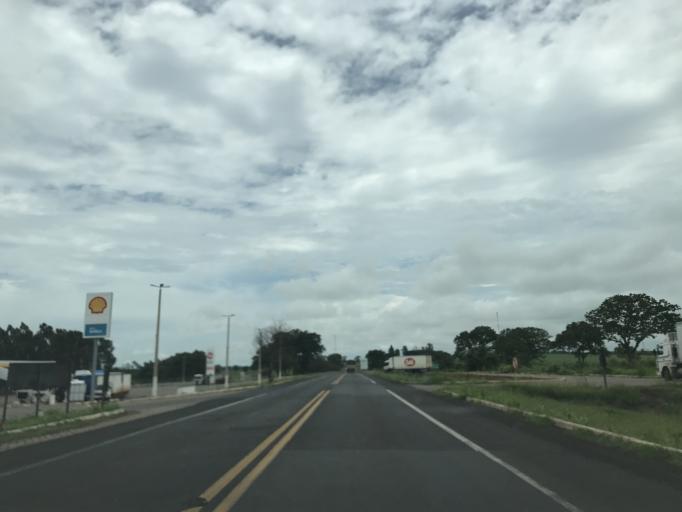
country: BR
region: Minas Gerais
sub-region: Frutal
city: Frutal
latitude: -19.8494
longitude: -48.9629
